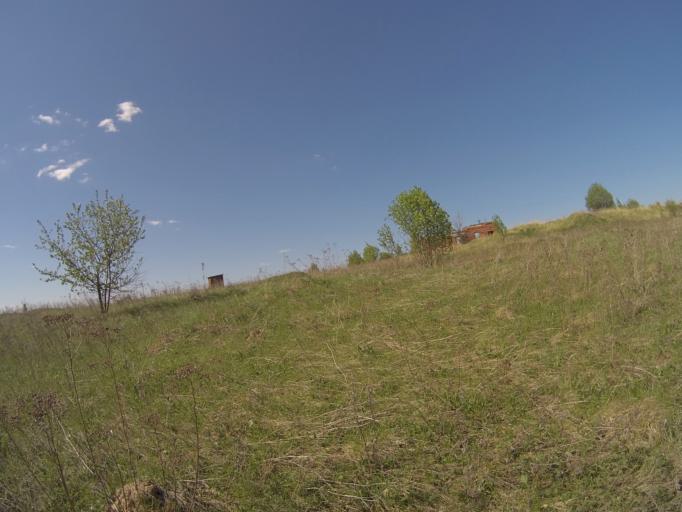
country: RU
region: Vladimir
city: Kideksha
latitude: 56.4160
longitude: 40.4867
